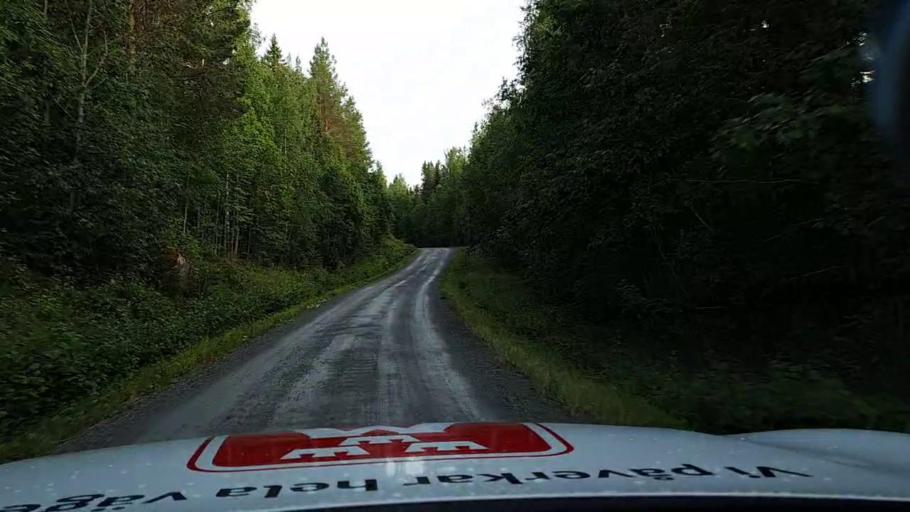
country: SE
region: Jaemtland
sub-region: Bergs Kommun
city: Hoverberg
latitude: 62.8476
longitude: 14.5675
